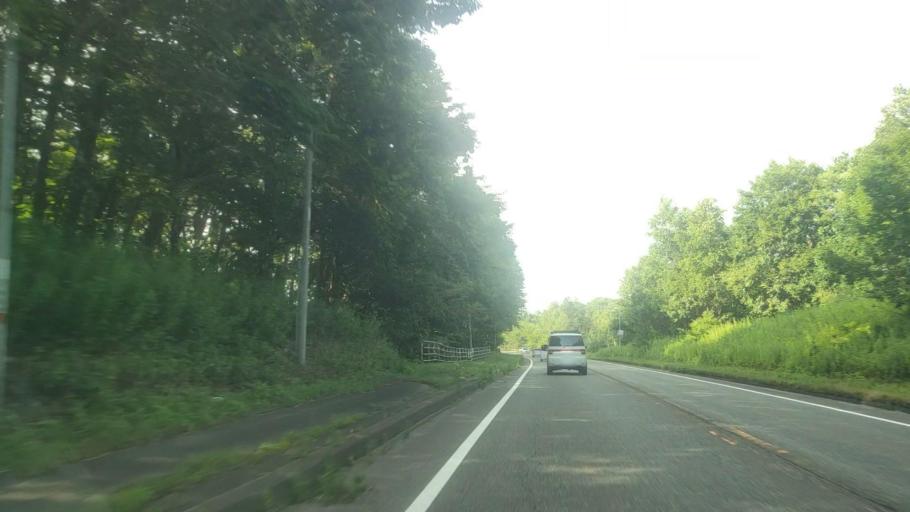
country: JP
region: Hokkaido
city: Chitose
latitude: 42.8716
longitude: 141.8224
